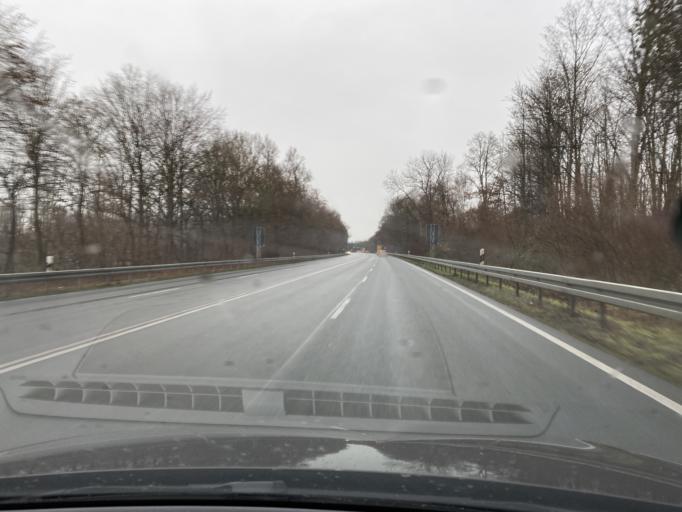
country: DE
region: North Rhine-Westphalia
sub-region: Regierungsbezirk Arnsberg
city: Lippstadt
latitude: 51.7071
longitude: 8.3586
